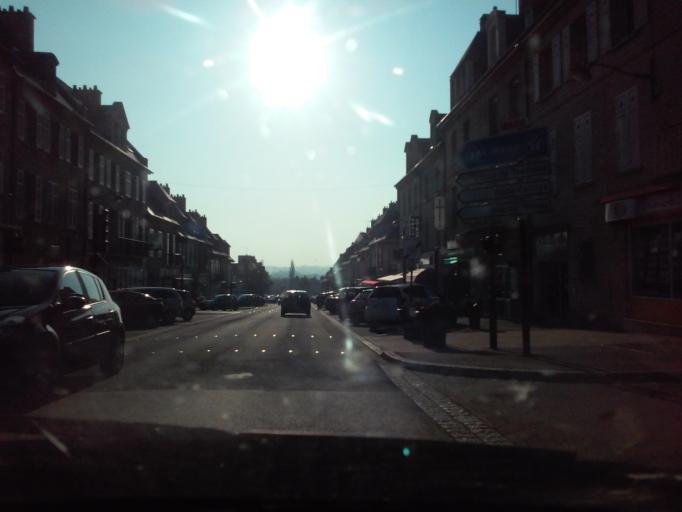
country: FR
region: Lower Normandy
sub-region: Departement du Calvados
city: Villers-Bocage
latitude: 49.0805
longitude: -0.6561
